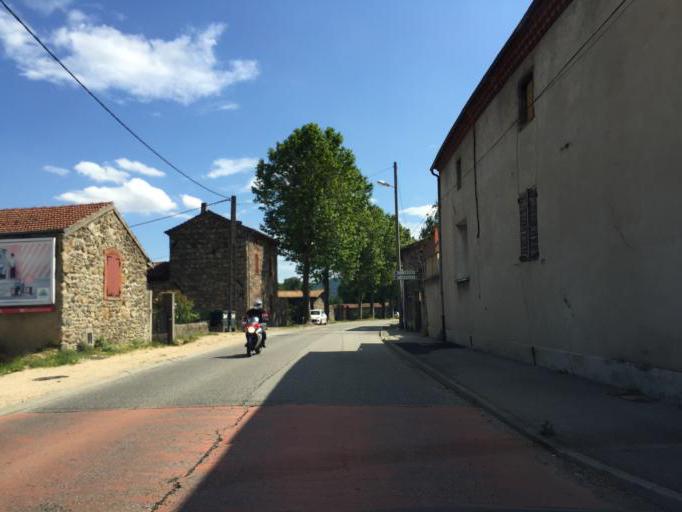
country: FR
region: Rhone-Alpes
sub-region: Departement de la Drome
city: Saint-Vallier
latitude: 45.1416
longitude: 4.8079
